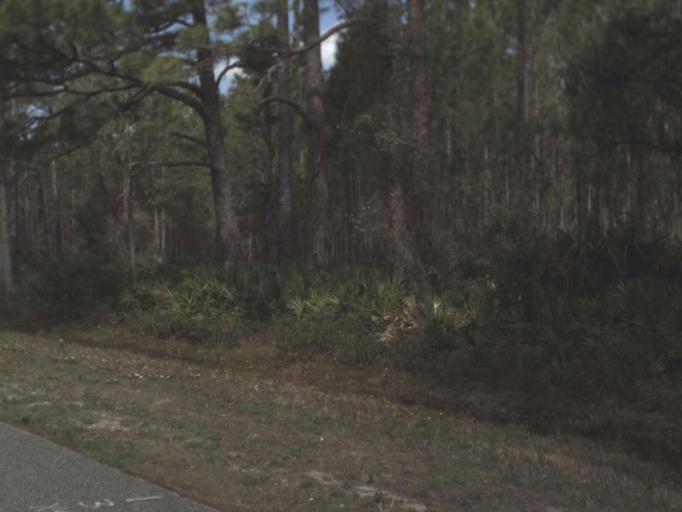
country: US
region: Florida
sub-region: Franklin County
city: Apalachicola
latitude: 29.7259
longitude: -85.1254
